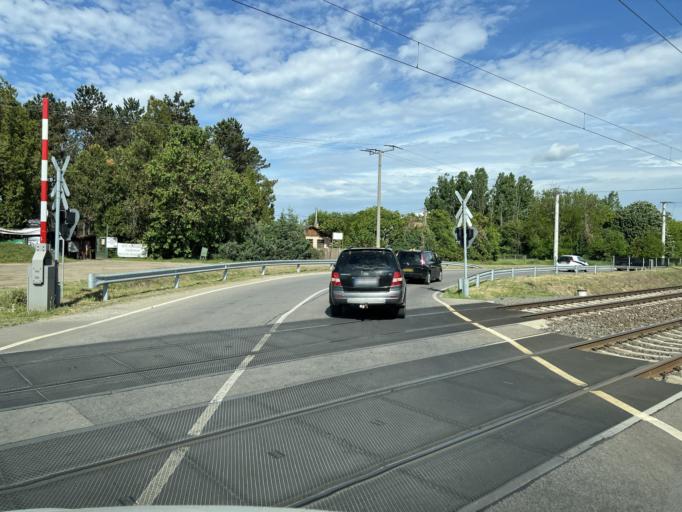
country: HU
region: Pest
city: Isaszeg
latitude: 47.5601
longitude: 19.3783
